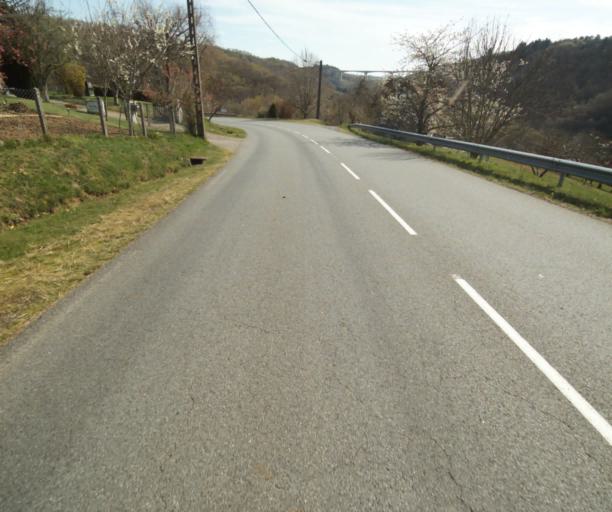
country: FR
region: Limousin
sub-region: Departement de la Correze
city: Naves
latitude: 45.3357
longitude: 1.7881
